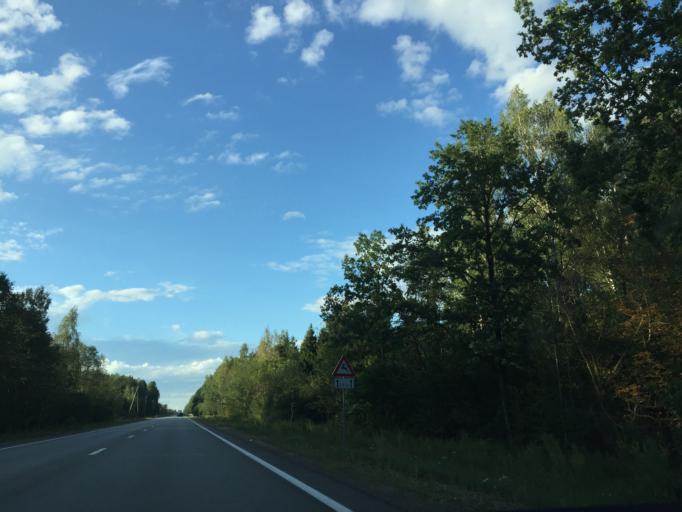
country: LV
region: Jelgava
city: Jelgava
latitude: 56.5480
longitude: 23.7092
